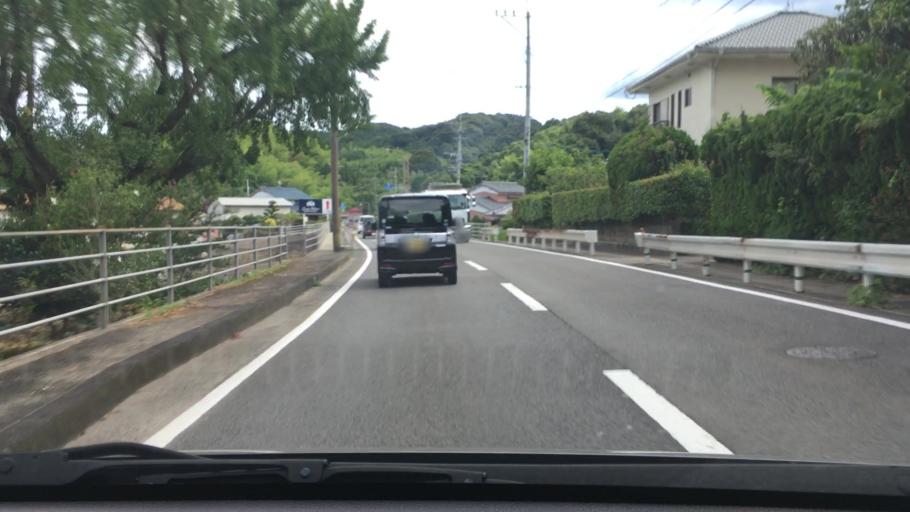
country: JP
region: Nagasaki
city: Togitsu
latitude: 32.9346
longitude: 129.7835
